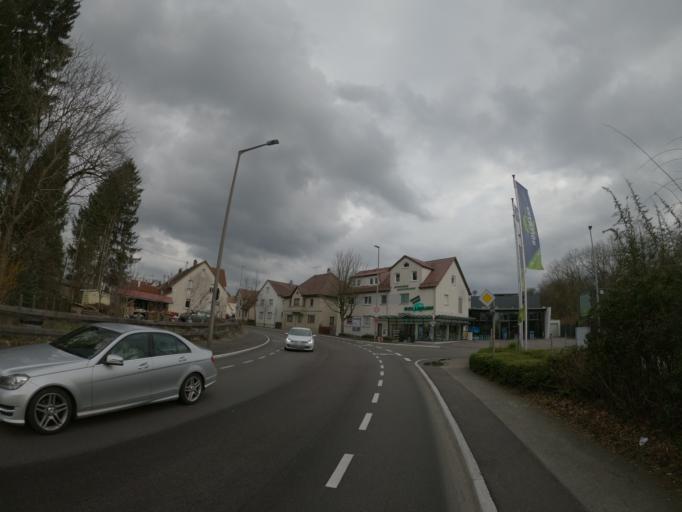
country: DE
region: Baden-Wuerttemberg
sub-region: Regierungsbezirk Stuttgart
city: Eislingen
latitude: 48.6882
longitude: 9.6839
